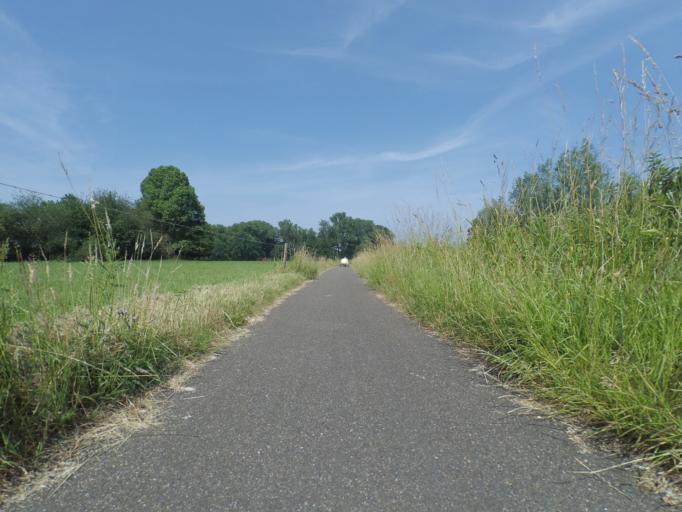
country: NL
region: North Brabant
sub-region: Gemeente Breda
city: Breda
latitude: 51.5279
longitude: 4.7796
